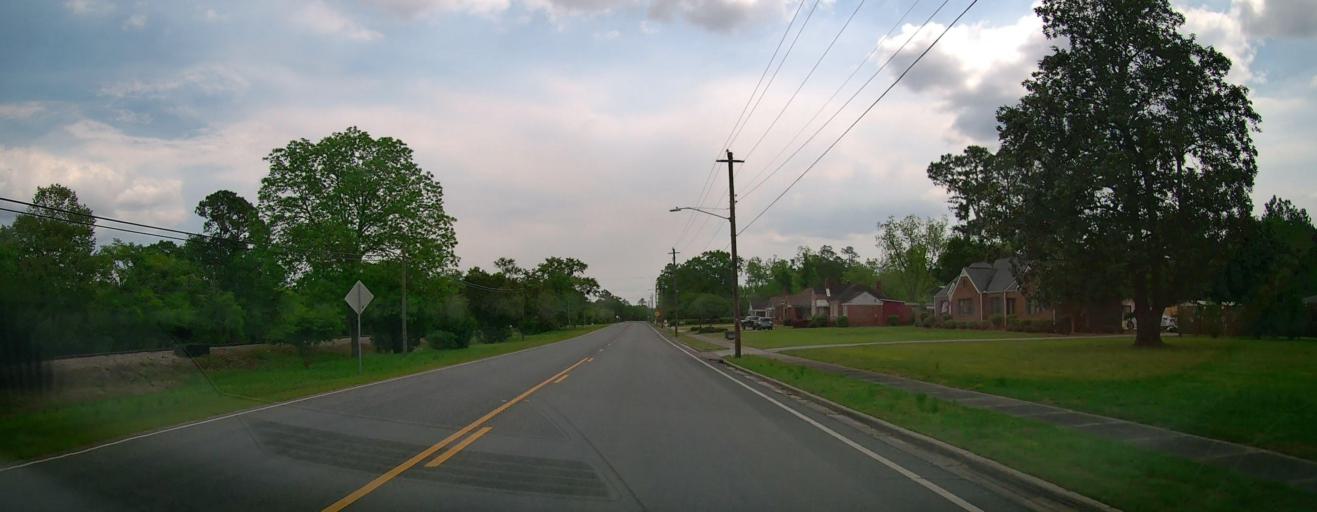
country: US
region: Georgia
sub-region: Treutlen County
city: Soperton
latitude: 32.3717
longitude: -82.5863
